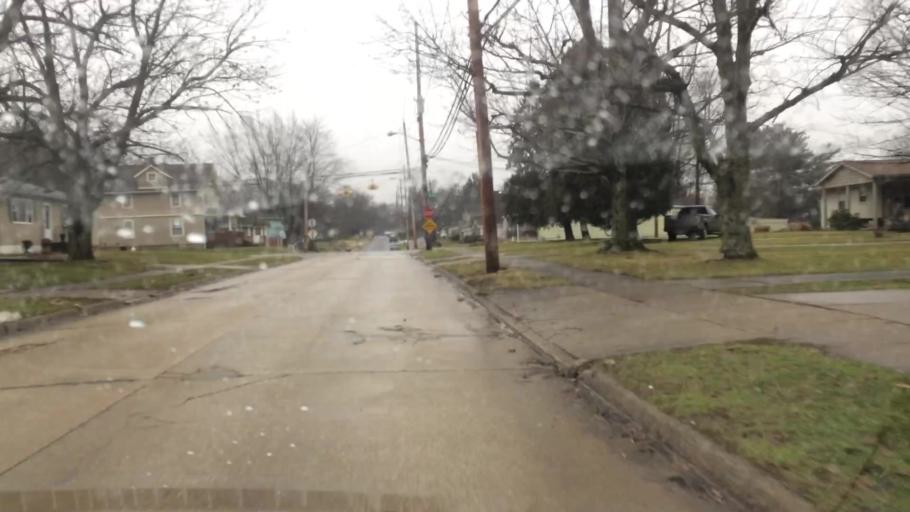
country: US
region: Ohio
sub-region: Summit County
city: Cuyahoga Falls
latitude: 41.1069
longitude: -81.4752
